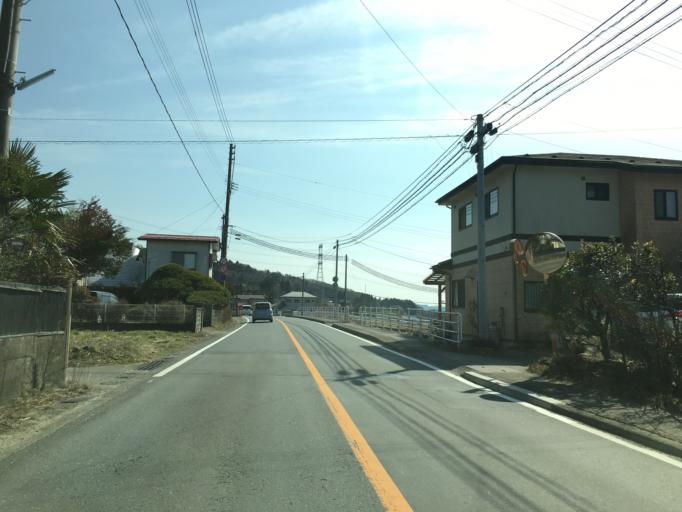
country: JP
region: Ibaraki
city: Daigo
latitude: 36.9388
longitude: 140.4131
